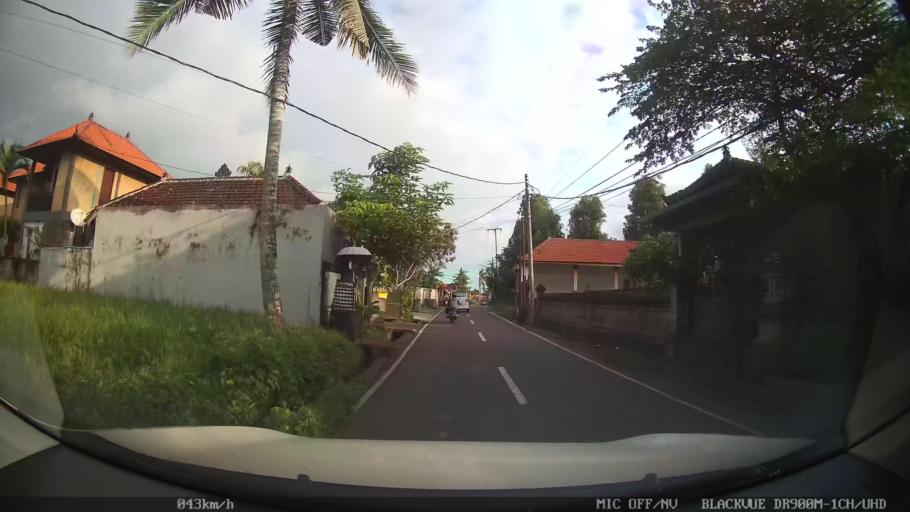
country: ID
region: Bali
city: Banjar Pande
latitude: -8.5138
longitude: 115.2503
